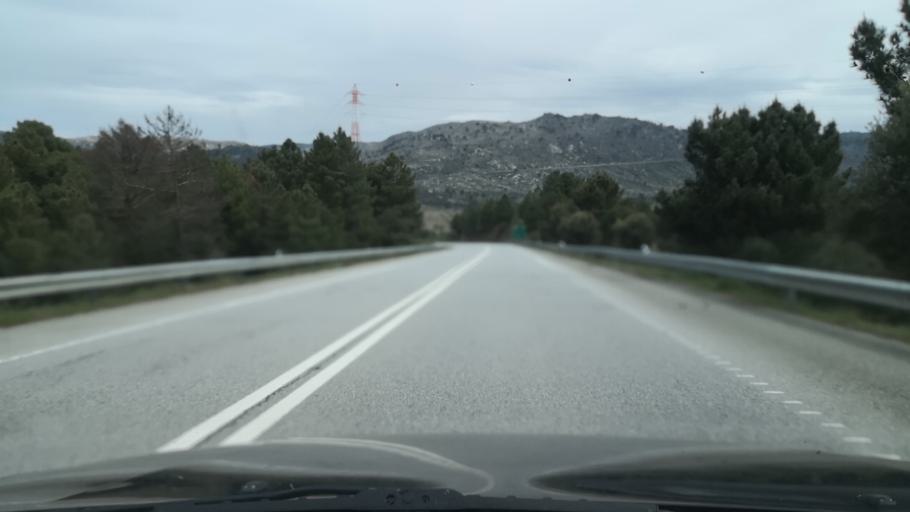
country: PT
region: Guarda
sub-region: Celorico da Beira
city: Celorico da Beira
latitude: 40.6233
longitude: -7.3046
